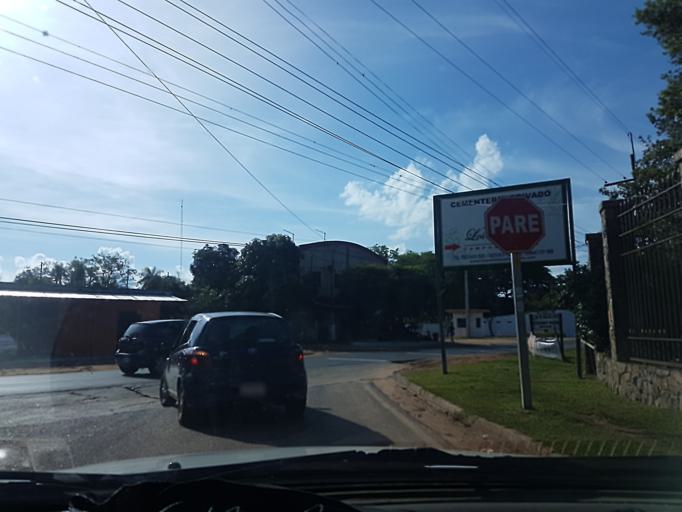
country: PY
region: Central
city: Limpio
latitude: -25.1910
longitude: -57.4635
